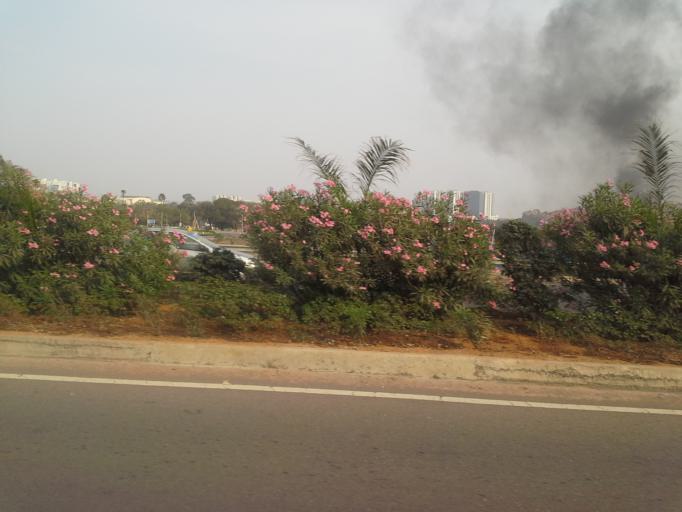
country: IN
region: Telangana
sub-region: Rangareddi
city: Kukatpalli
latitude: 17.4186
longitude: 78.3561
